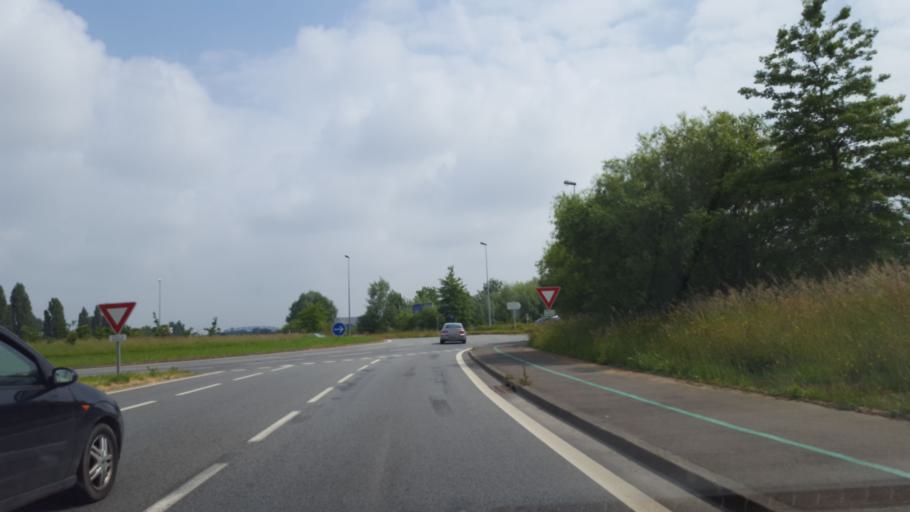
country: FR
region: Brittany
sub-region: Departement d'Ille-et-Vilaine
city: Chartres-de-Bretagne
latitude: 48.0555
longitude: -1.7035
